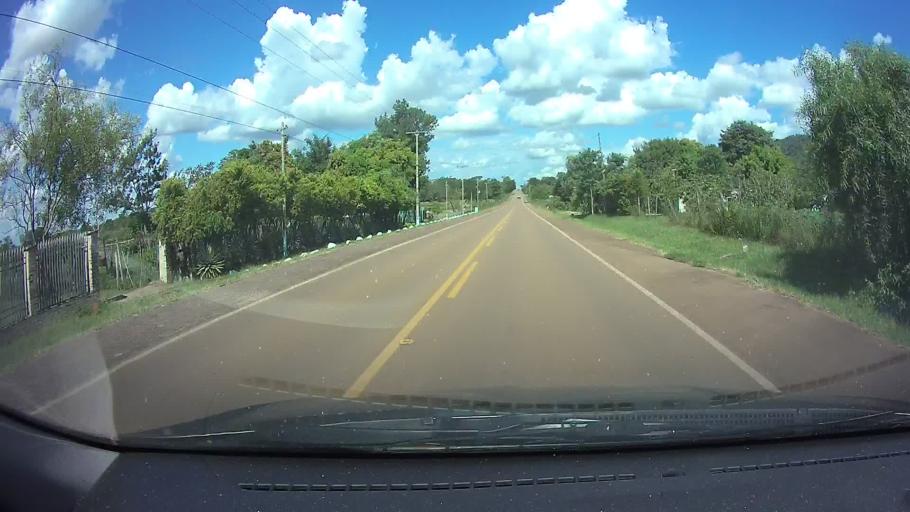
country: PY
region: Paraguari
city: La Colmena
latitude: -25.9111
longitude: -56.7562
